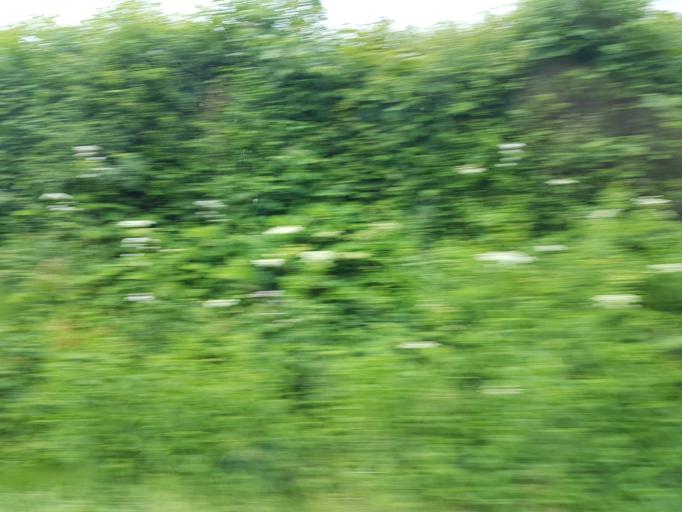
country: FR
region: Bourgogne
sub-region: Departement de la Nievre
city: Lormes
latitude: 47.1628
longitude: 3.8418
